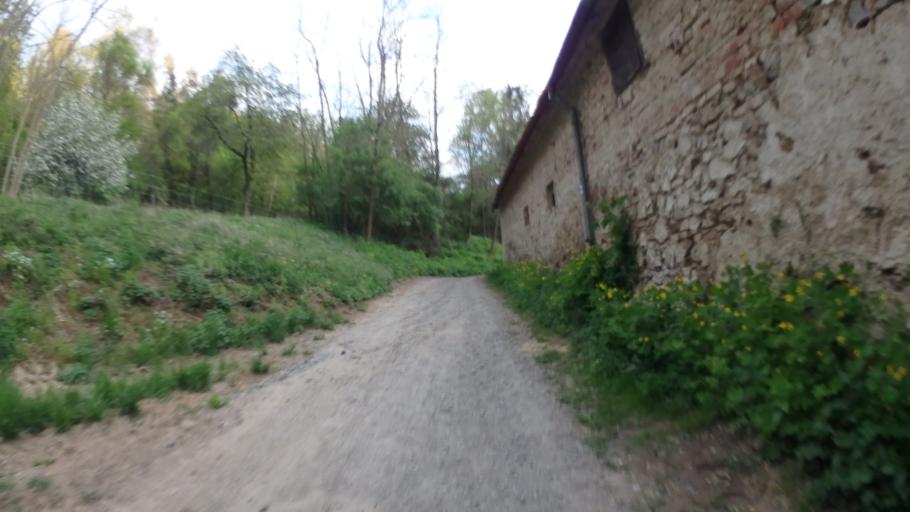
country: CZ
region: South Moravian
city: Strelice
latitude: 49.1426
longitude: 16.4771
